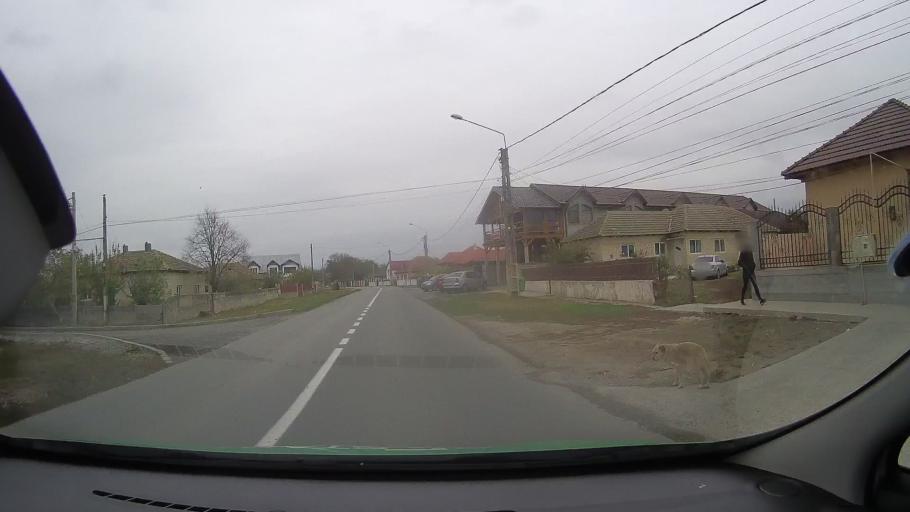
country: RO
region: Constanta
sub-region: Comuna Mihail Kogalniceanu
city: Mihail Kogalniceanu
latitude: 44.3771
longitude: 28.4653
